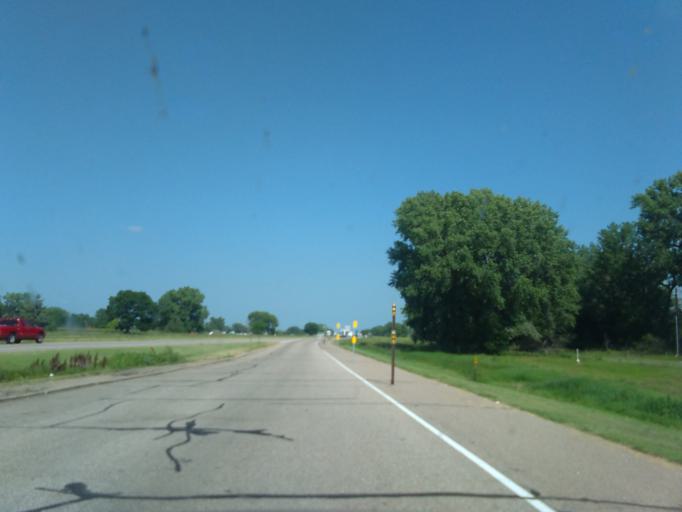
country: US
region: Nebraska
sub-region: Buffalo County
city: Kearney
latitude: 40.6705
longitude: -99.1561
